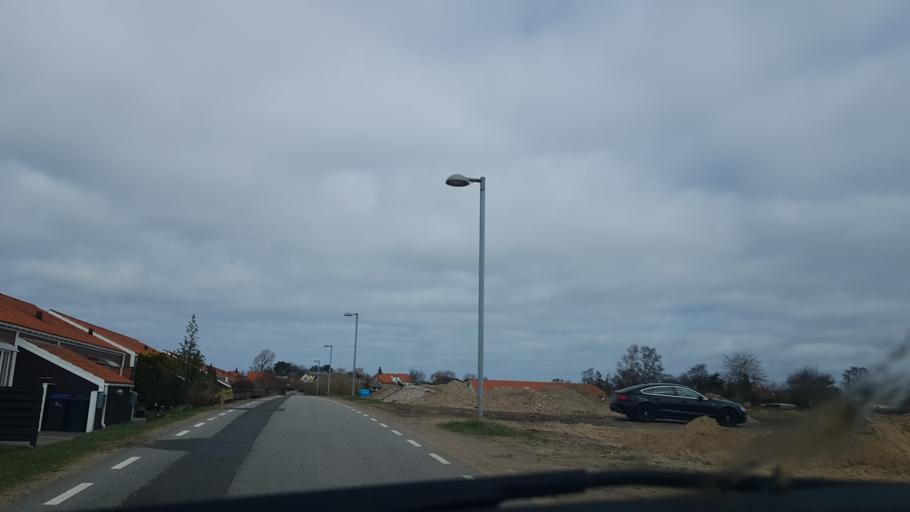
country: DK
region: Zealand
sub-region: Odsherred Kommune
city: Hojby
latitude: 55.9072
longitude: 11.5906
